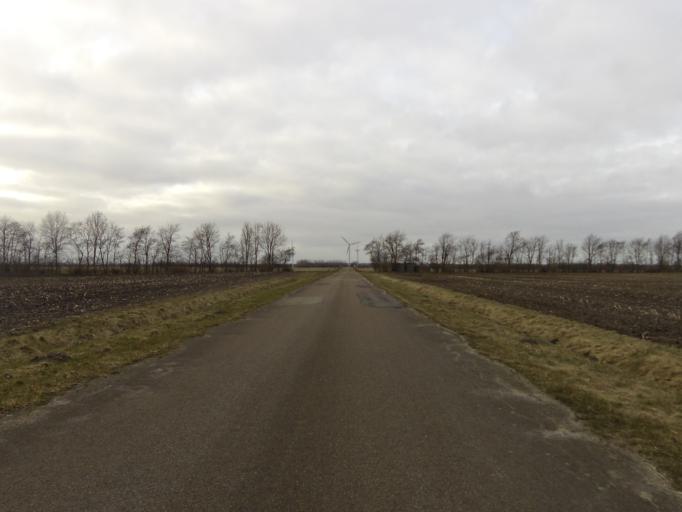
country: DK
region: South Denmark
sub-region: Tonder Kommune
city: Toftlund
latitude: 55.2381
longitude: 9.0732
